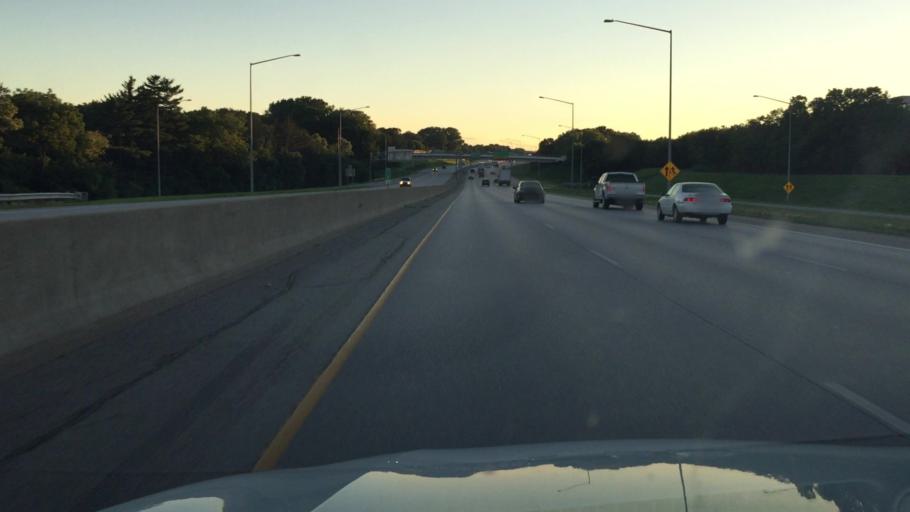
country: US
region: Iowa
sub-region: Polk County
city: Clive
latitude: 41.5928
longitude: -93.7375
